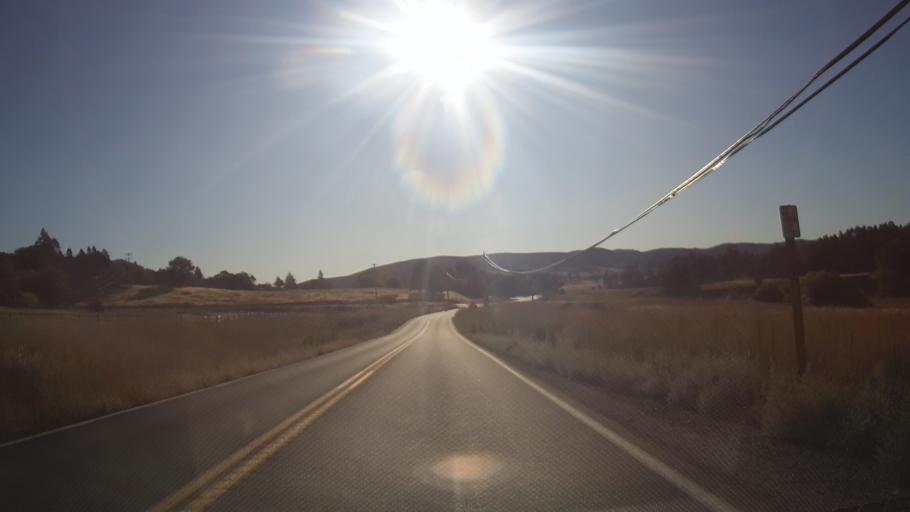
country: US
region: California
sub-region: San Diego County
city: Julian
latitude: 32.9914
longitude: -116.5826
